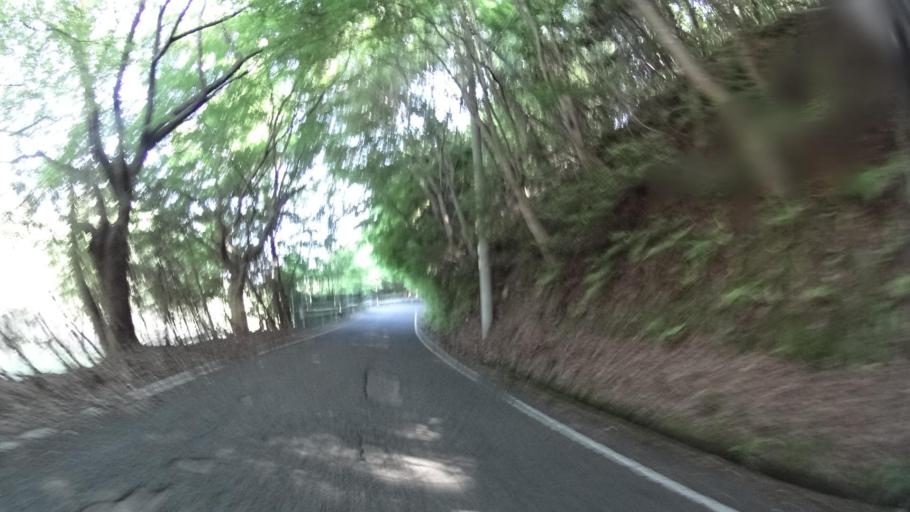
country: JP
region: Kyoto
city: Kameoka
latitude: 35.0023
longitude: 135.5619
